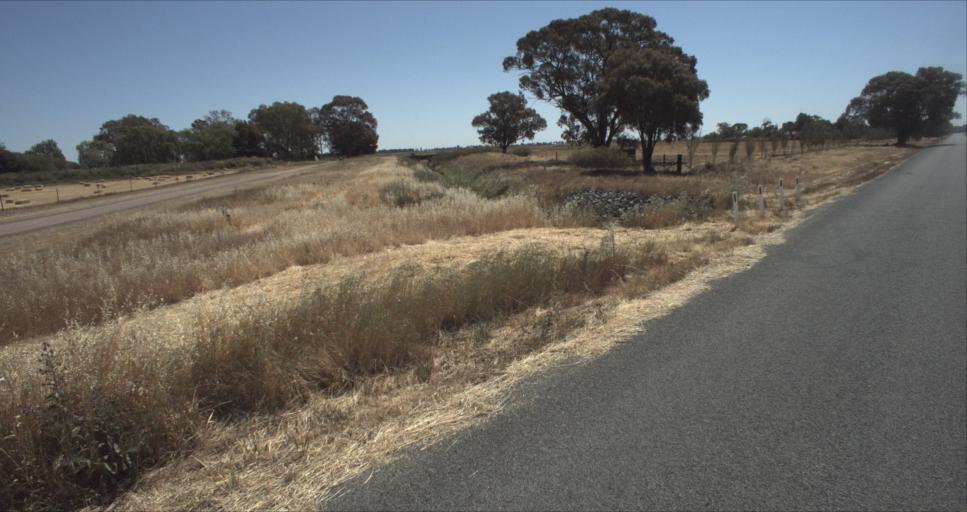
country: AU
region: New South Wales
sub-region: Leeton
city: Leeton
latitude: -34.5308
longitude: 146.4458
